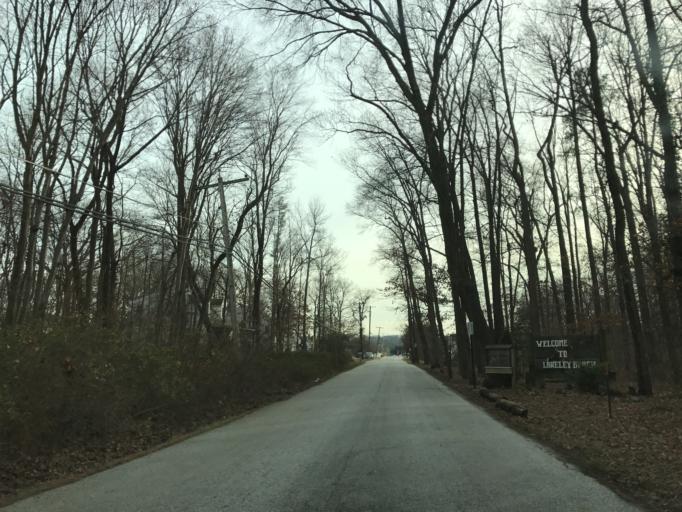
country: US
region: Maryland
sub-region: Baltimore County
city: White Marsh
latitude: 39.3887
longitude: -76.4143
